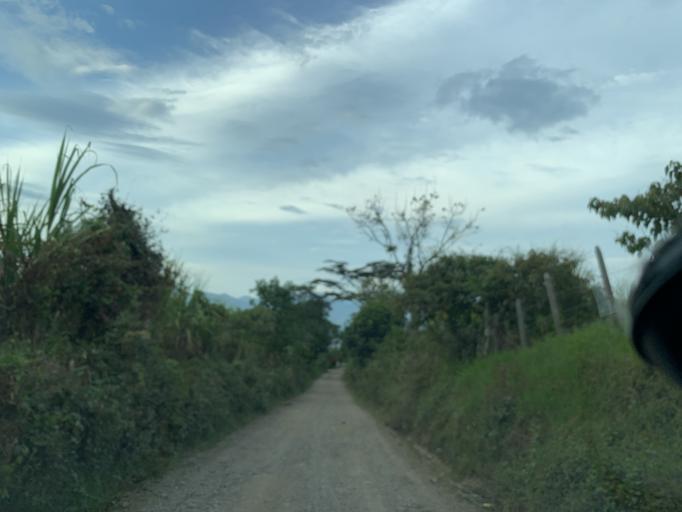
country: CO
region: Boyaca
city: Santana
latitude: 6.0658
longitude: -73.4835
